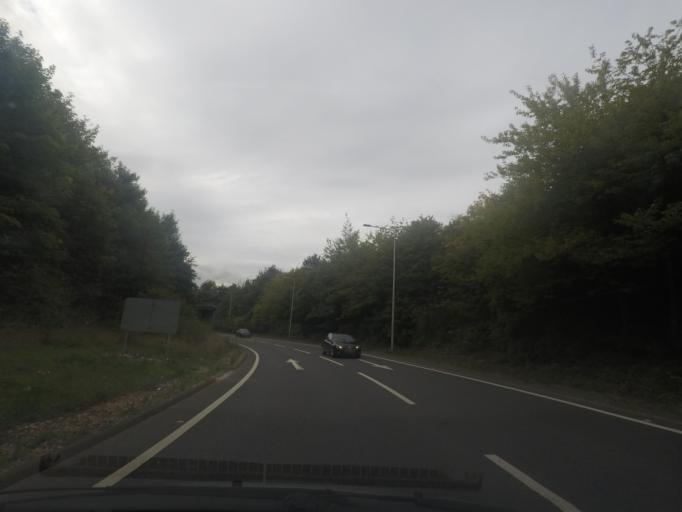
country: GB
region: England
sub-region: Hampshire
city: Kings Worthy
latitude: 51.1760
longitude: -1.3371
